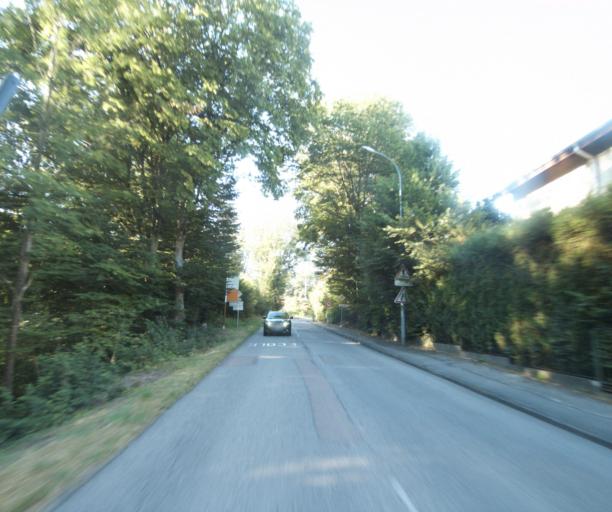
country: FR
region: Lorraine
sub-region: Departement des Vosges
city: Chantraine
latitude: 48.1468
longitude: 6.4550
